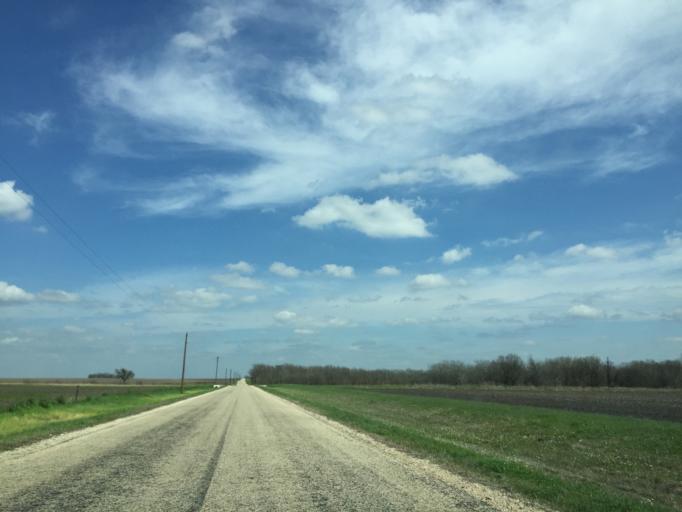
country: US
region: Texas
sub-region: Milam County
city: Thorndale
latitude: 30.5512
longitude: -97.2647
